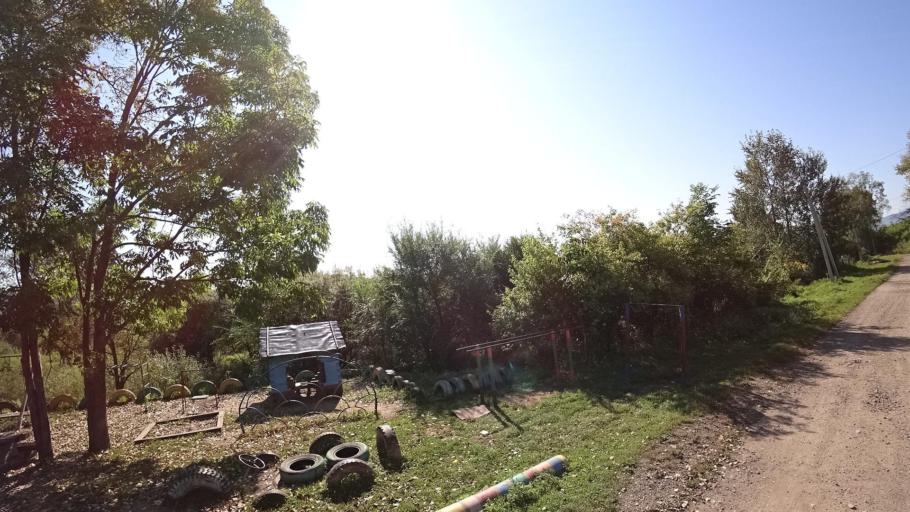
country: RU
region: Jewish Autonomous Oblast
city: Bira
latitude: 49.0037
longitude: 132.4728
